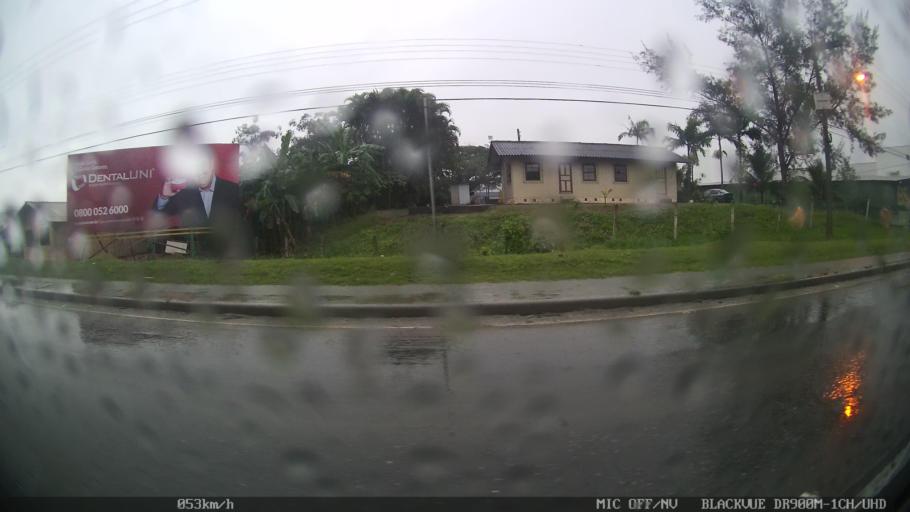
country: BR
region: Santa Catarina
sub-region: Itajai
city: Itajai
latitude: -26.8758
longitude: -48.7276
